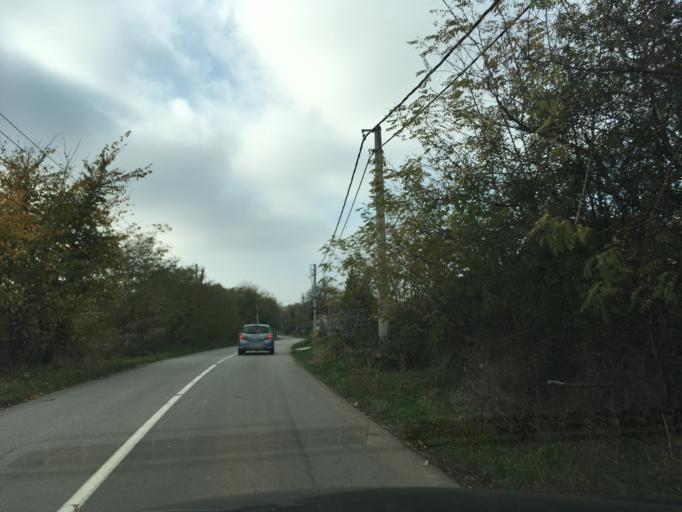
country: RS
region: Central Serbia
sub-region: Belgrade
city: Sopot
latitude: 44.4949
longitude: 20.6103
